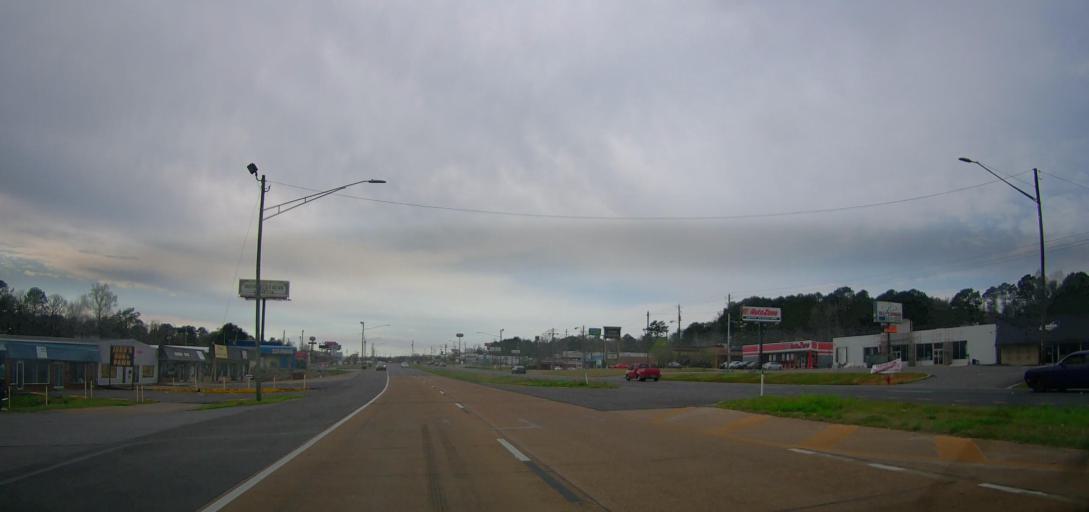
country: US
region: Alabama
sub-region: Walker County
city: Jasper
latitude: 33.8494
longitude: -87.2745
